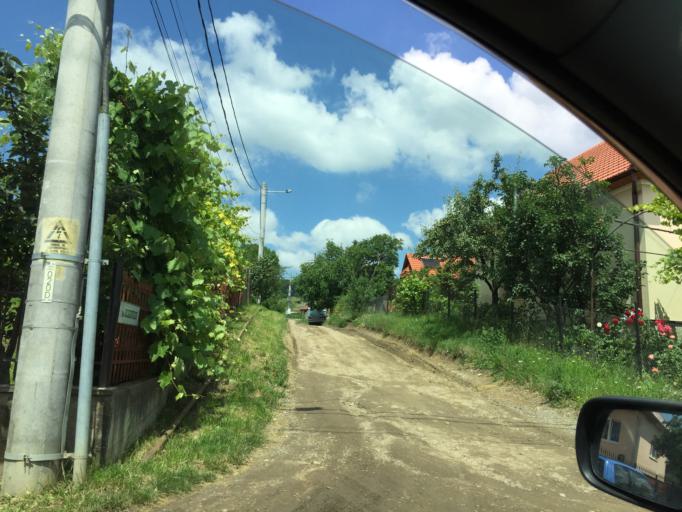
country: RO
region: Cluj
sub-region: Municipiul Cluj-Napoca
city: Cluj-Napoca
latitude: 46.7963
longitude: 23.5703
